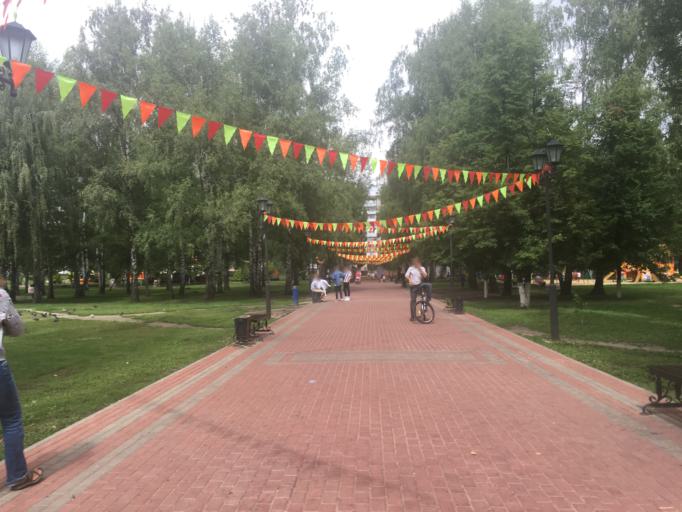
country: RU
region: Voronezj
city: Rossosh'
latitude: 50.1960
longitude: 39.5766
